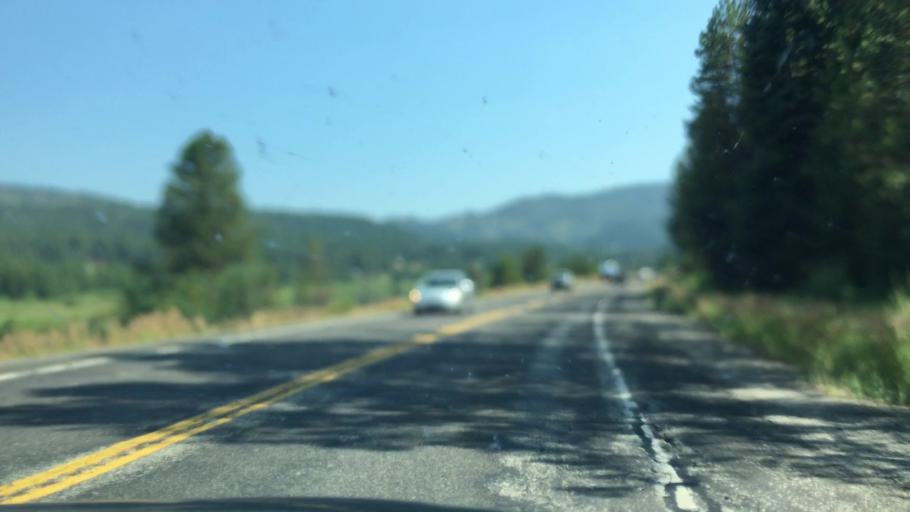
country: US
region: Idaho
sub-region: Valley County
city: Cascade
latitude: 44.2959
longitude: -116.0847
